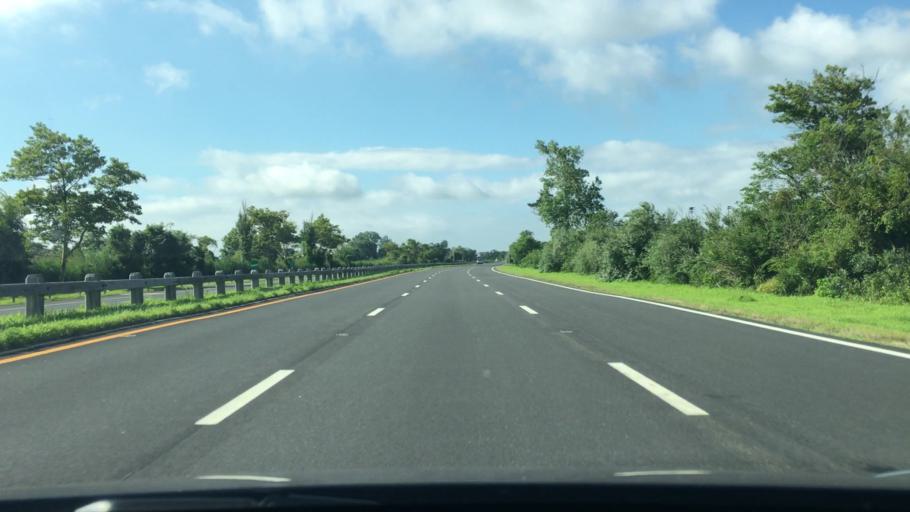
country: US
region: New York
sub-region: Nassau County
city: Bellmore
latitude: 40.6502
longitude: -73.5098
